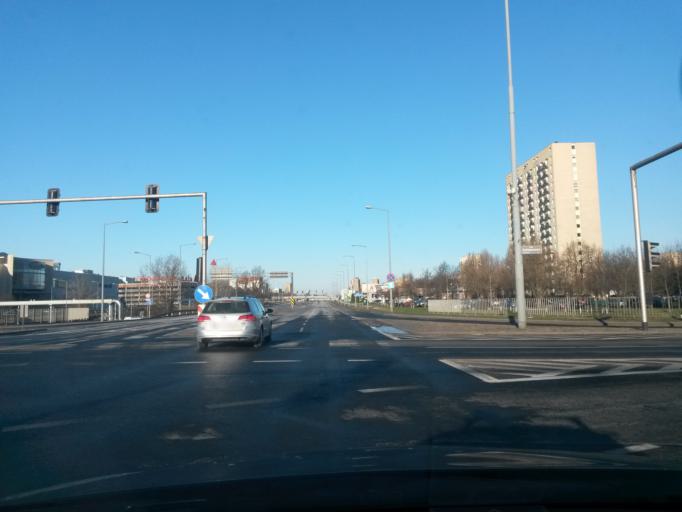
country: PL
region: Greater Poland Voivodeship
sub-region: Poznan
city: Poznan
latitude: 52.4359
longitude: 16.9211
